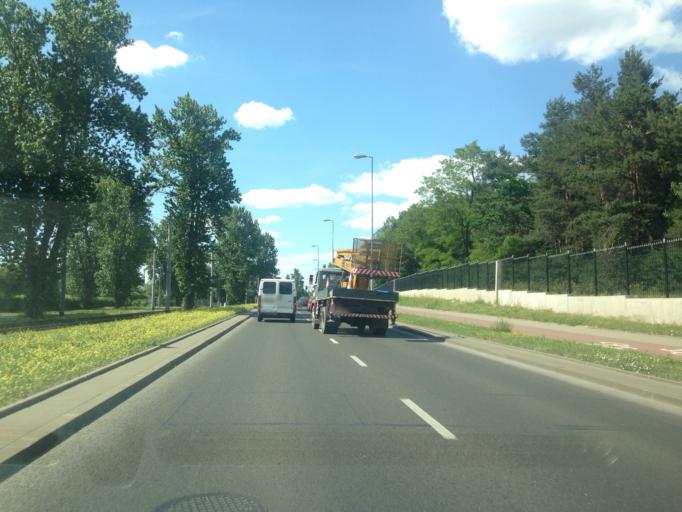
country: PL
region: Masovian Voivodeship
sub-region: Warszawa
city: Praga Polnoc
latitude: 52.2716
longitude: 21.0343
